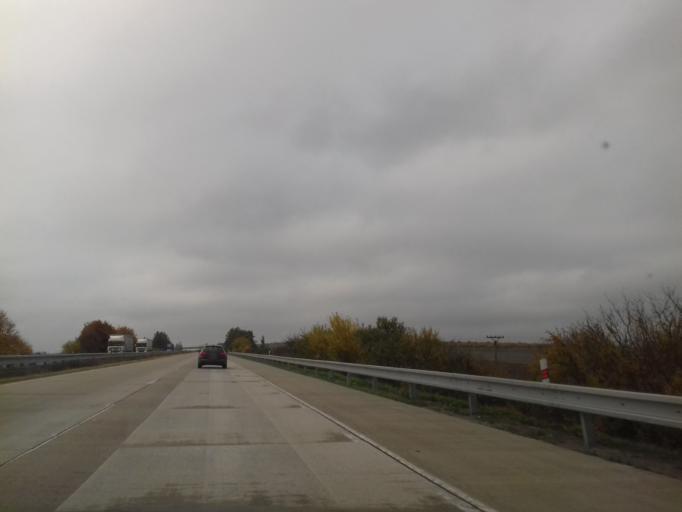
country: CZ
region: South Moravian
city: Velke Pavlovice
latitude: 48.8853
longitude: 16.8100
